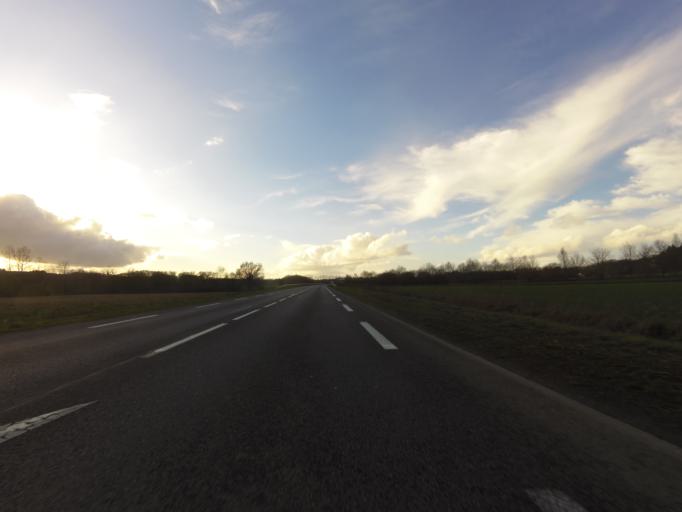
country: FR
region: Brittany
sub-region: Departement du Morbihan
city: Lanouee
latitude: 47.9622
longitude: -2.6016
